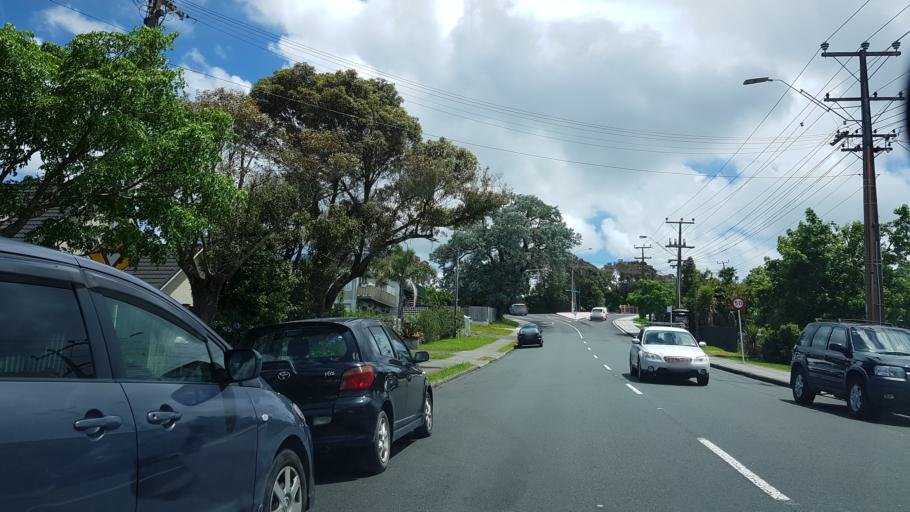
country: NZ
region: Auckland
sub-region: Auckland
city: North Shore
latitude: -36.8002
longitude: 174.7375
